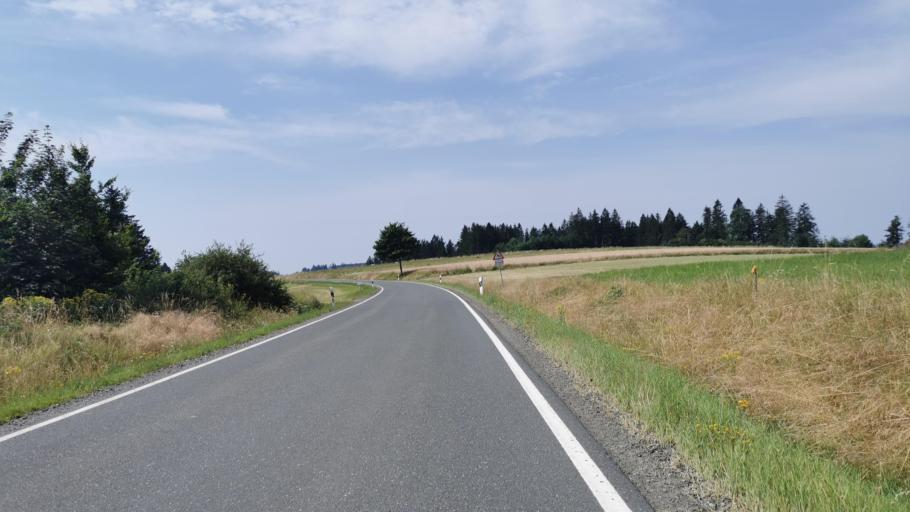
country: DE
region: Bavaria
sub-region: Upper Franconia
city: Wilhelmsthal
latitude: 50.3182
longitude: 11.4107
